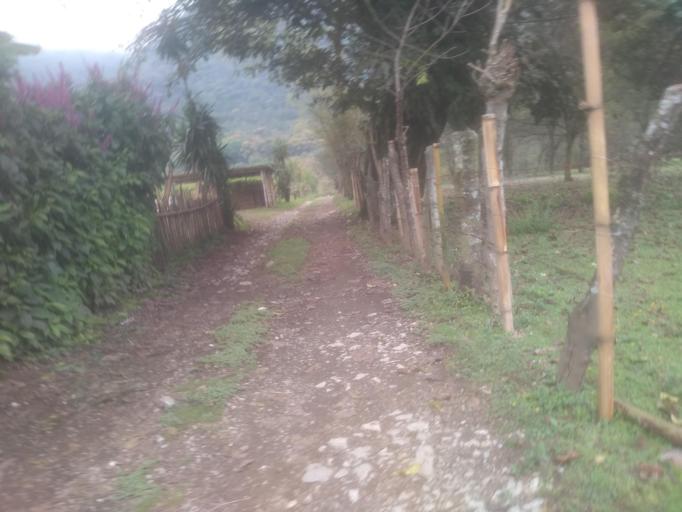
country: MX
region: Veracruz
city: Chocaman
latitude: 19.0009
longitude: -97.0424
